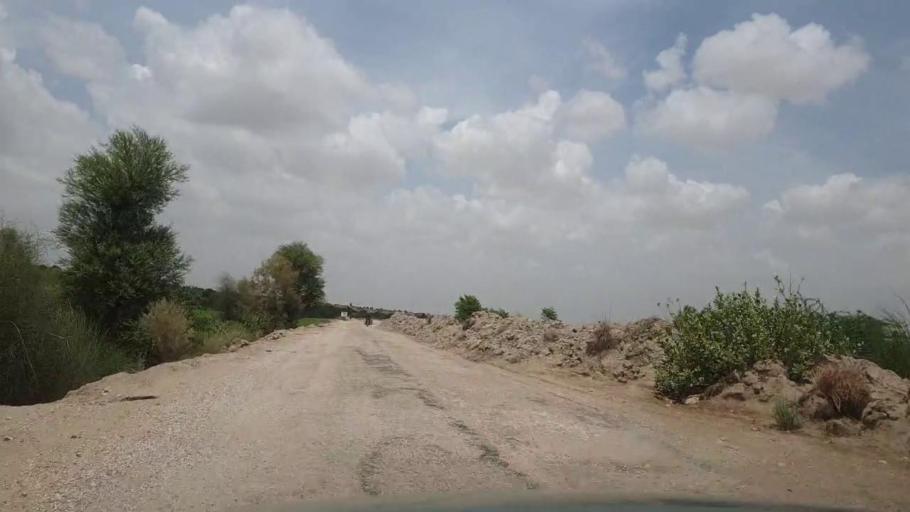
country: PK
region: Sindh
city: Kot Diji
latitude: 27.2157
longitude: 69.1001
